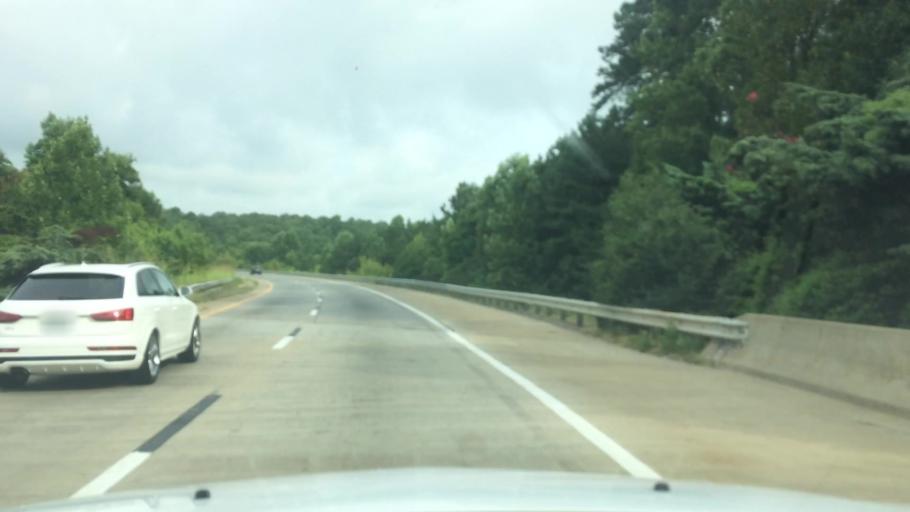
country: US
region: North Carolina
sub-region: Orange County
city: Hillsborough
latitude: 36.0595
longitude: -79.1262
